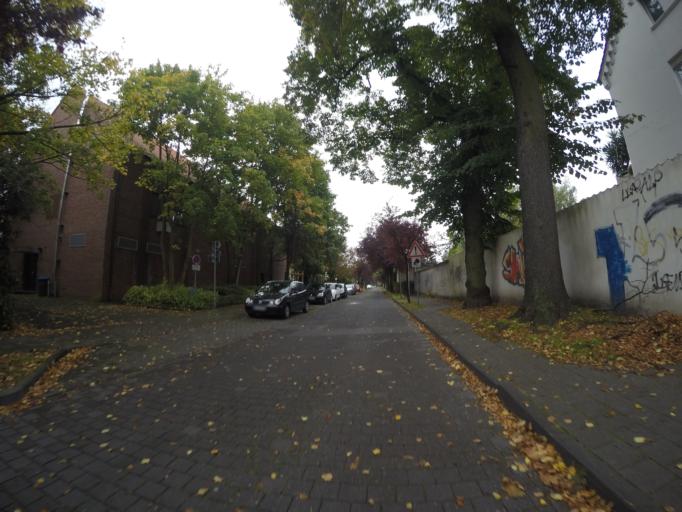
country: DE
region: North Rhine-Westphalia
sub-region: Regierungsbezirk Arnsberg
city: Lippstadt
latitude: 51.6735
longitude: 8.3513
